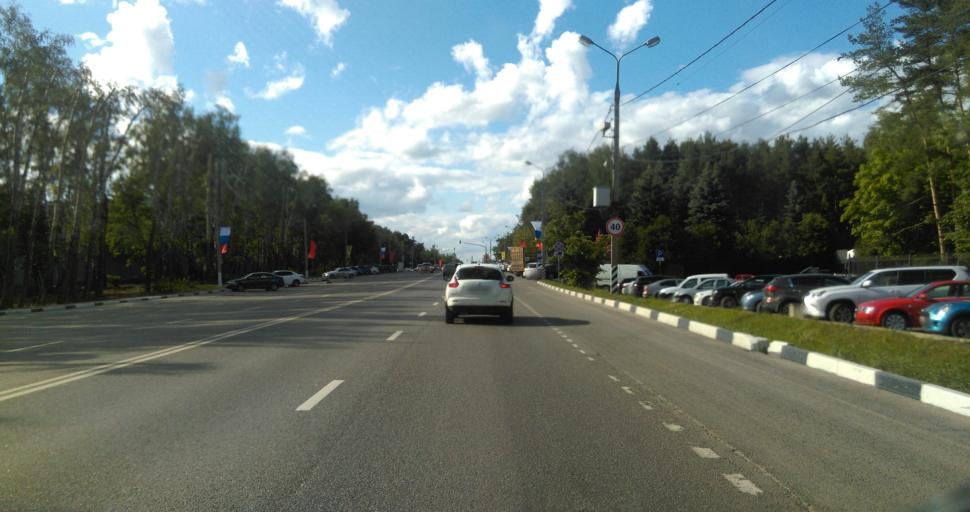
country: RU
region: Moskovskaya
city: Domodedovo
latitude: 55.4177
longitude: 37.7785
